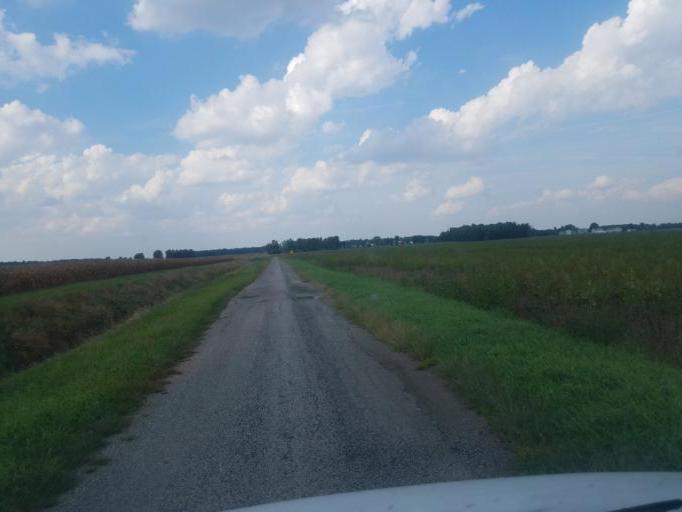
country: US
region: Ohio
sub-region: Hancock County
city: Arlington
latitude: 40.8024
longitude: -83.6897
